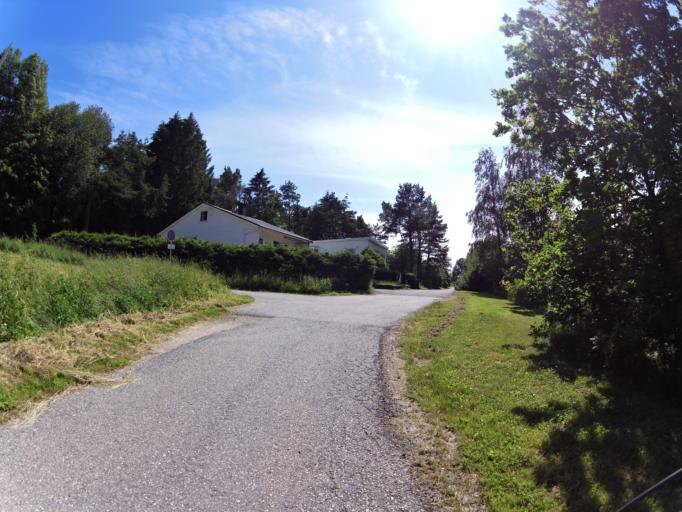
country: NO
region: Ostfold
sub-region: Fredrikstad
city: Fredrikstad
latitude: 59.2362
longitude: 10.9661
